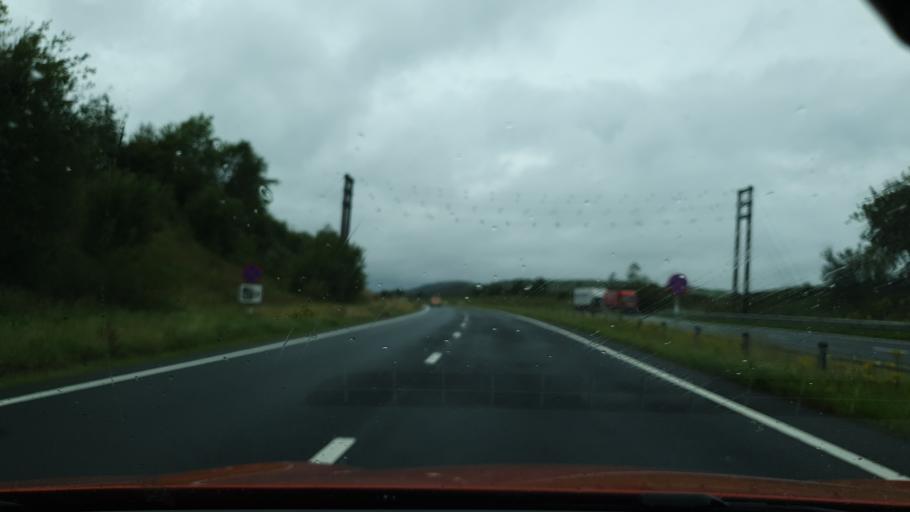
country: GB
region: England
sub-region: Cumbria
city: Grange-over-Sands
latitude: 54.2317
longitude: -2.9152
